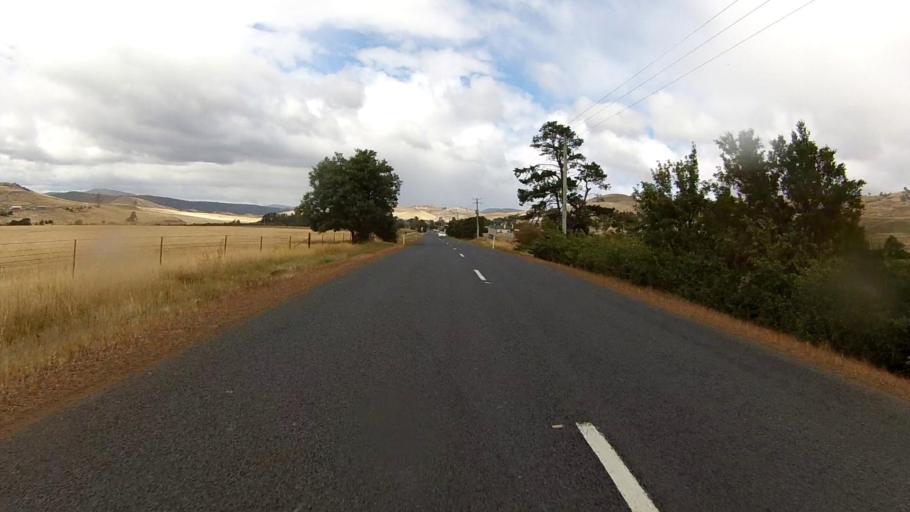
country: AU
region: Tasmania
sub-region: Brighton
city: Bridgewater
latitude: -42.5285
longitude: 147.3599
